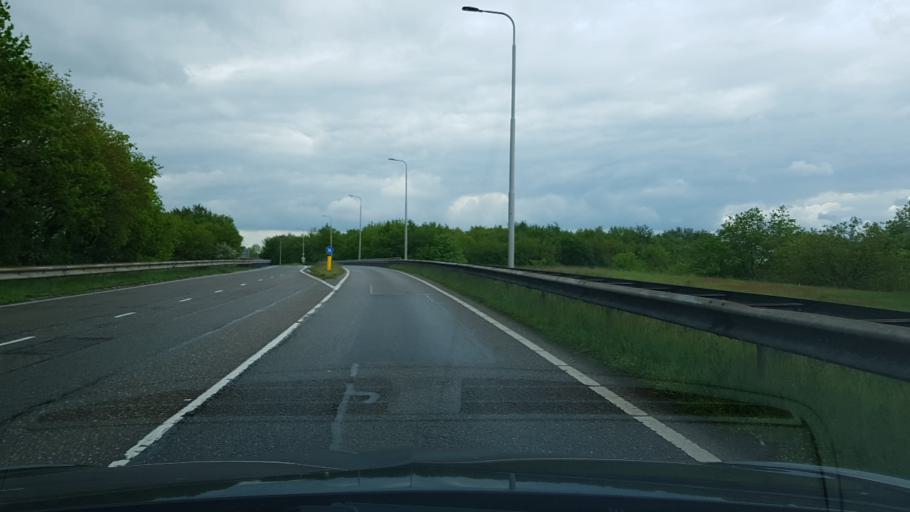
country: NL
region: North Holland
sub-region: Gemeente Laren
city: Laren
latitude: 52.2531
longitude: 5.2470
